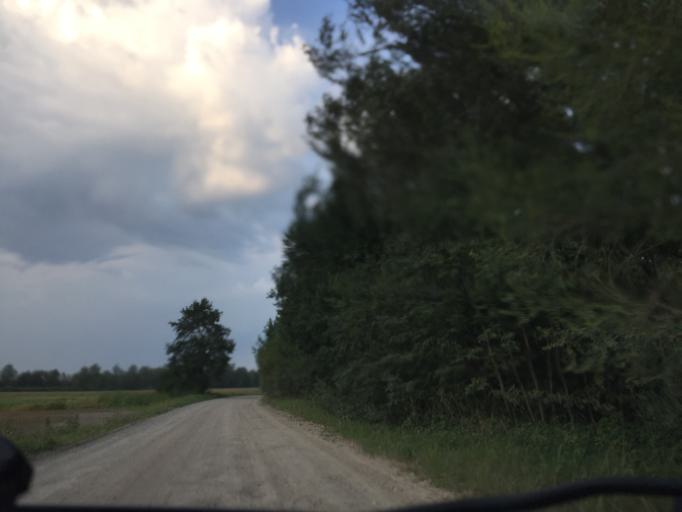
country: LV
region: Dobeles Rajons
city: Dobele
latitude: 56.6166
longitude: 23.3588
